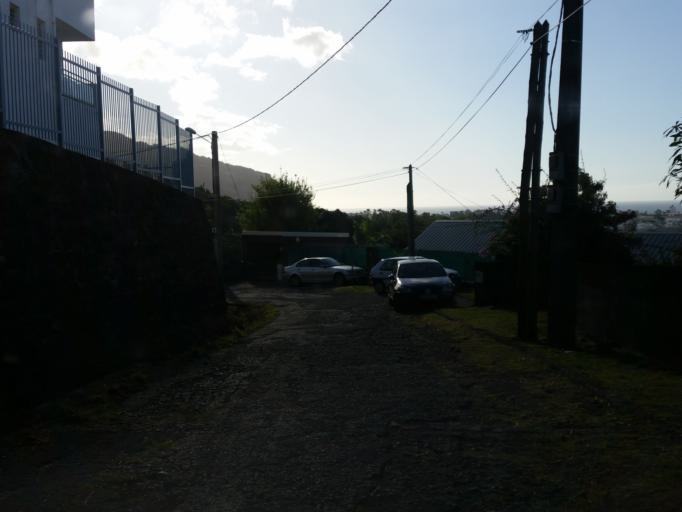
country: RE
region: Reunion
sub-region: Reunion
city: Saint-Denis
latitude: -20.8997
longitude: 55.4575
